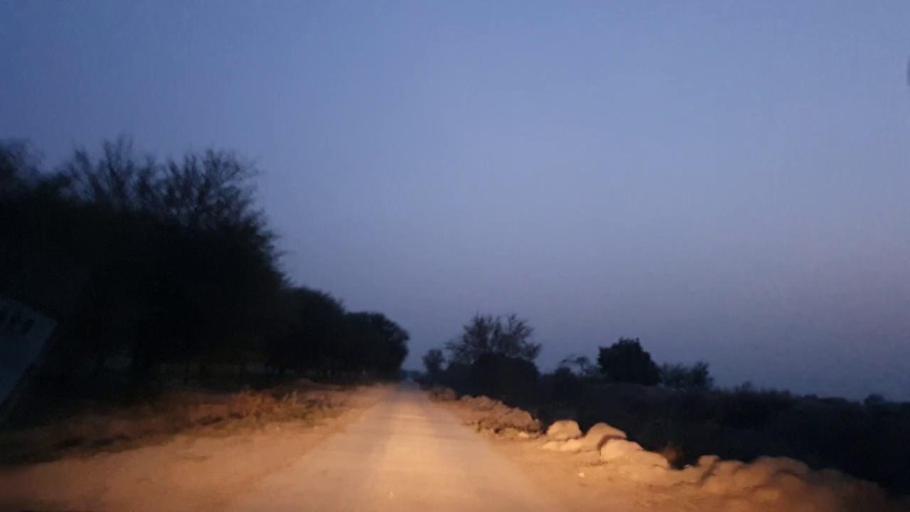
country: PK
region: Sindh
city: Tando Ghulam Ali
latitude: 25.0900
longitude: 68.9179
